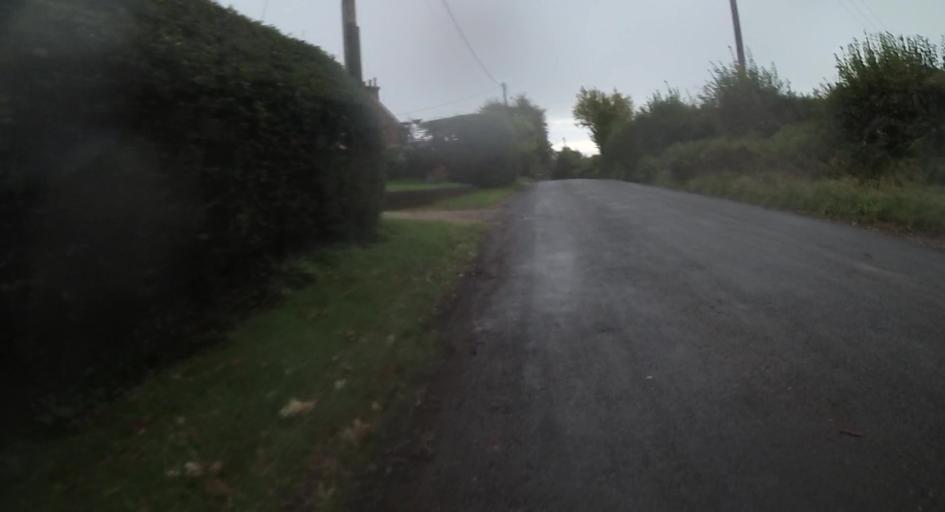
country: GB
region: England
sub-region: Hampshire
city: Tadley
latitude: 51.3069
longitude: -1.1339
